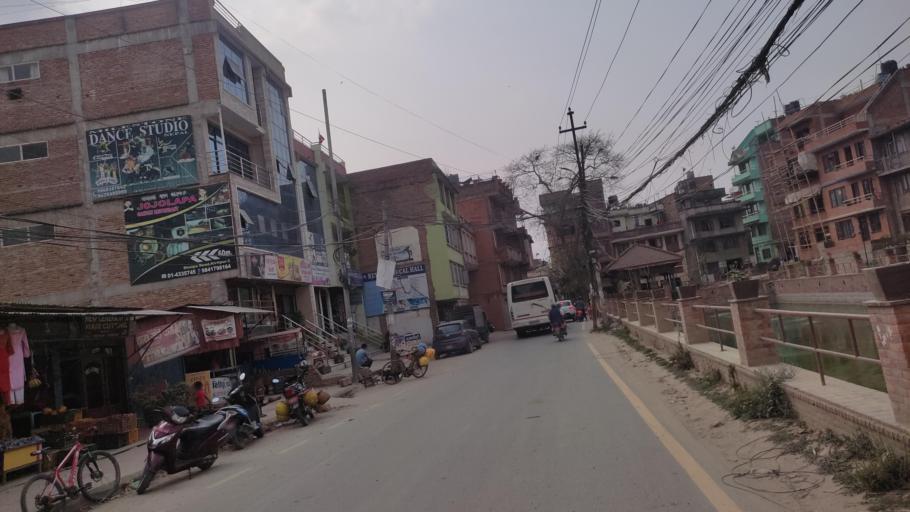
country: NP
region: Central Region
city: Kirtipur
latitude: 27.6781
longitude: 85.2737
